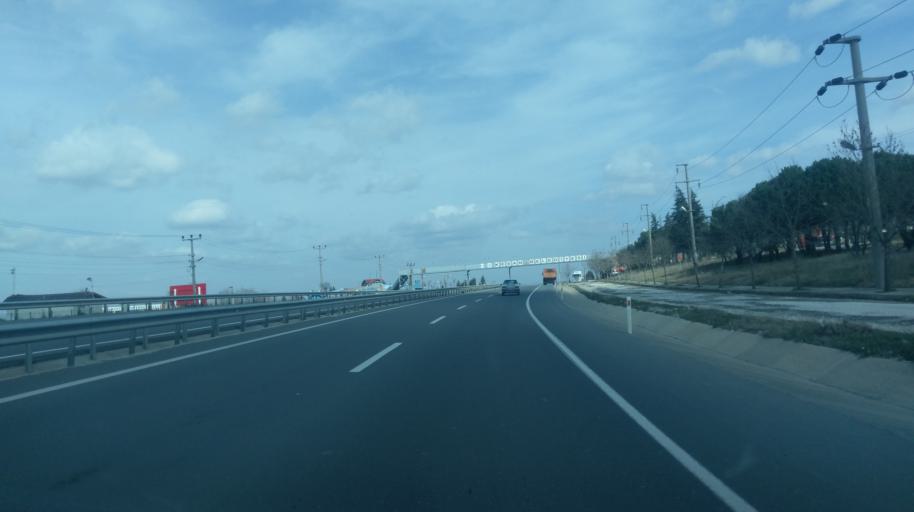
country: TR
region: Edirne
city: Kesan
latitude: 40.8653
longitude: 26.6236
